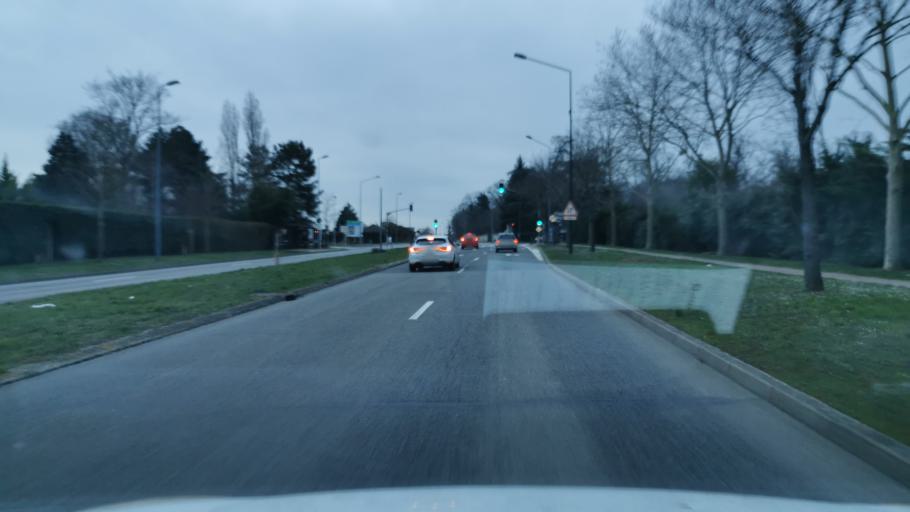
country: FR
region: Ile-de-France
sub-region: Departement des Yvelines
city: Magnanville
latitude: 48.9715
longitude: 1.6860
